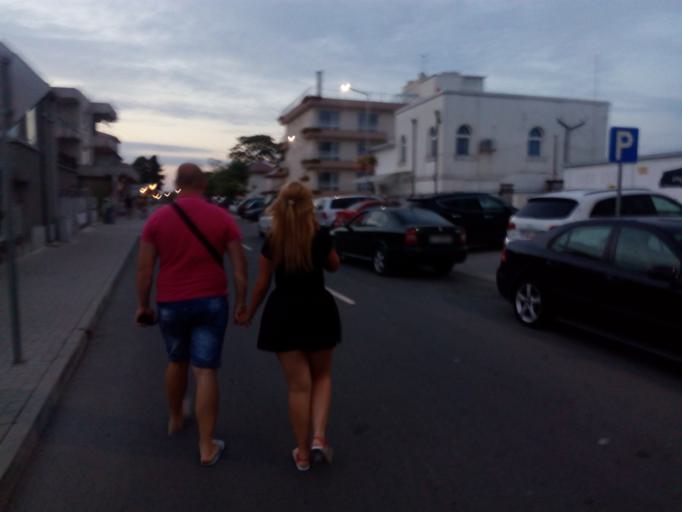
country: BG
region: Burgas
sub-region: Obshtina Nesebur
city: Obzor
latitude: 42.8181
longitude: 27.8845
